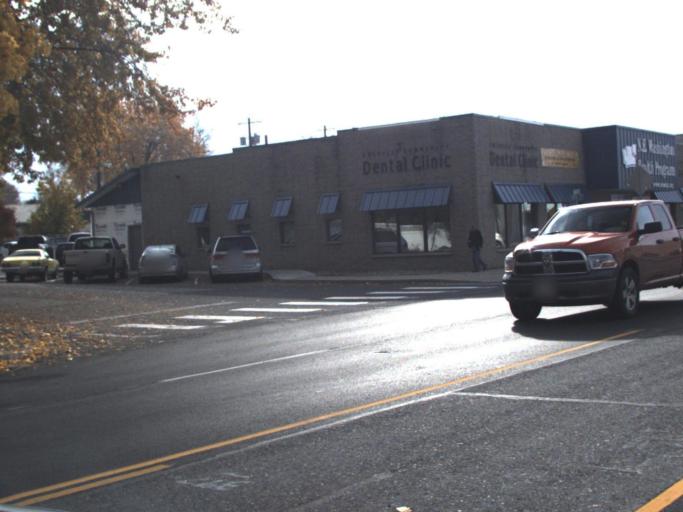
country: US
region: Washington
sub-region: Stevens County
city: Colville
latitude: 48.5477
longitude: -117.9058
